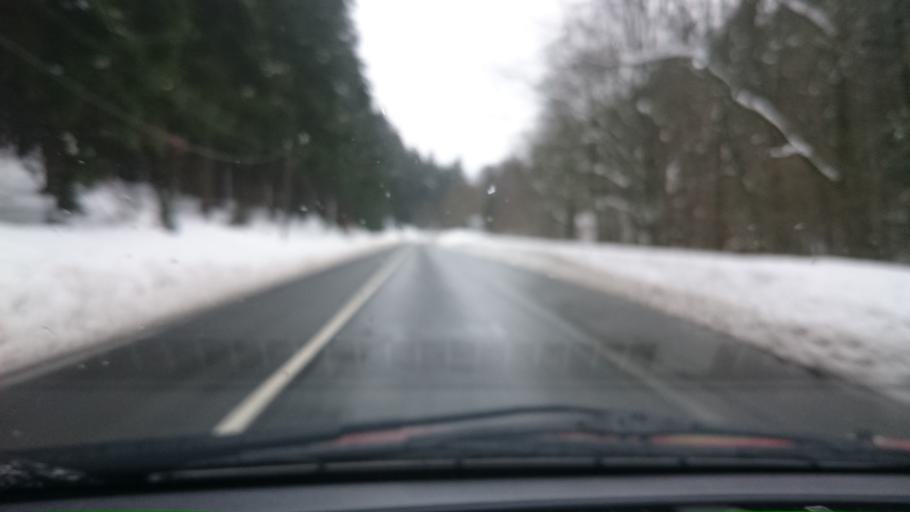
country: DE
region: Saxony
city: Tannenbergsthal
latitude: 50.4233
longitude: 12.4720
